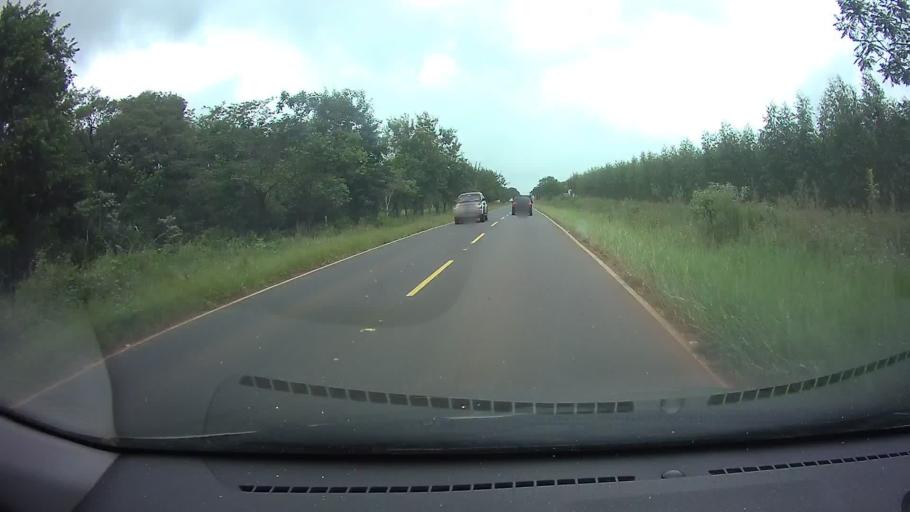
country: PY
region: Paraguari
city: Carapegua
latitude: -25.7479
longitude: -57.2683
